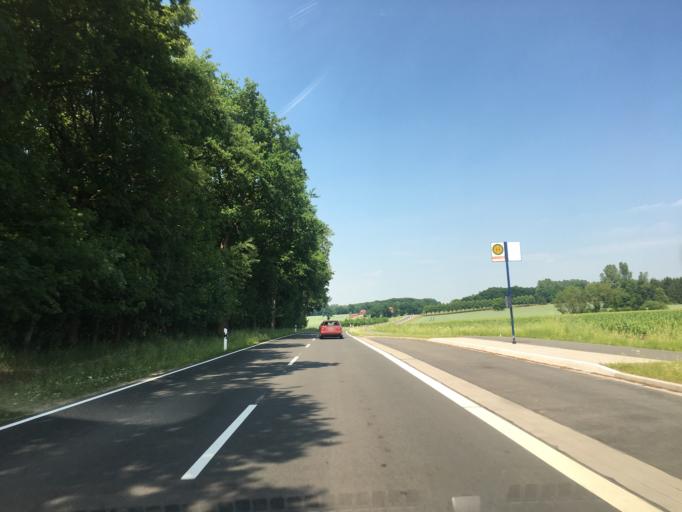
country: DE
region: North Rhine-Westphalia
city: Olfen
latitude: 51.7235
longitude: 7.4030
